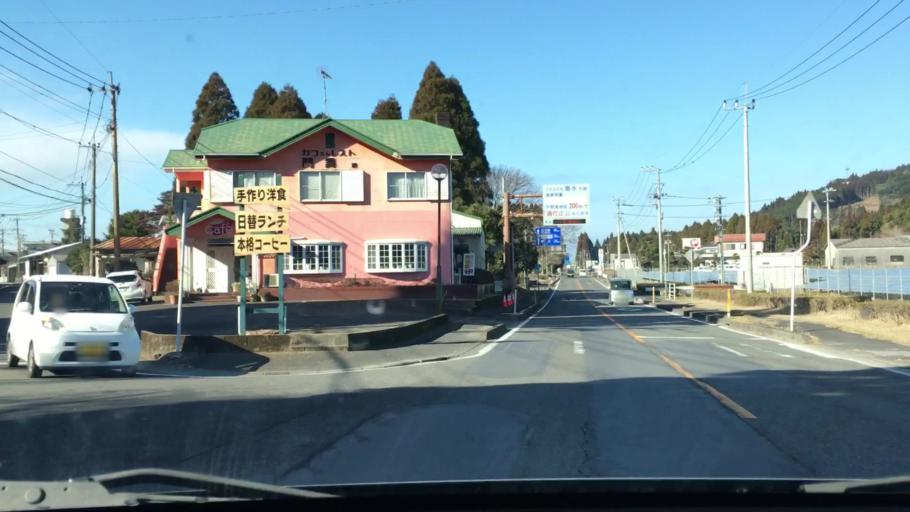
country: JP
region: Kagoshima
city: Kokubu-matsuki
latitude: 31.6720
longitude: 130.8560
